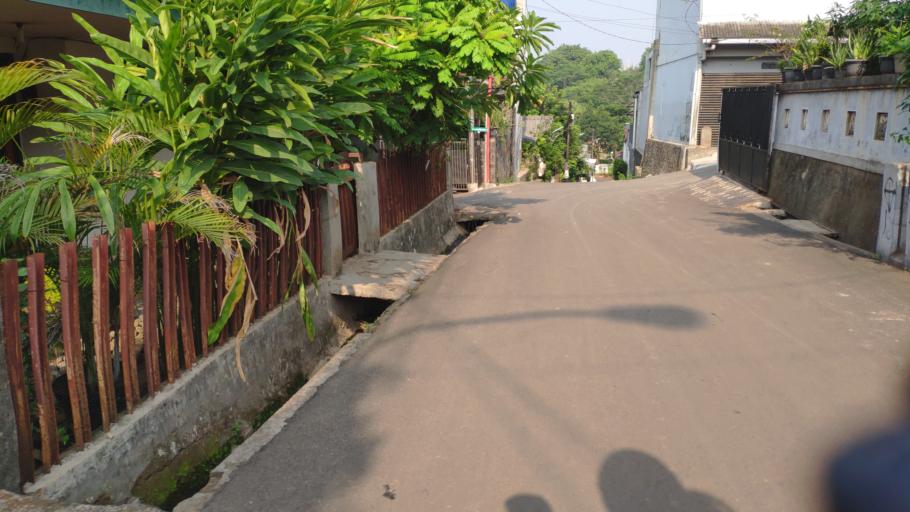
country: ID
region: West Java
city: Pamulang
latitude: -6.3022
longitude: 106.8059
